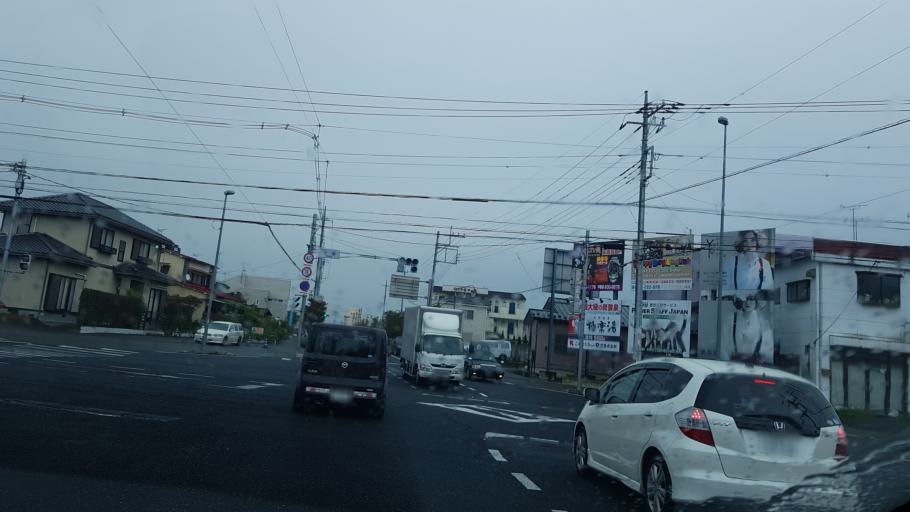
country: JP
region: Tochigi
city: Utsunomiya-shi
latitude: 36.5840
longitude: 139.9113
